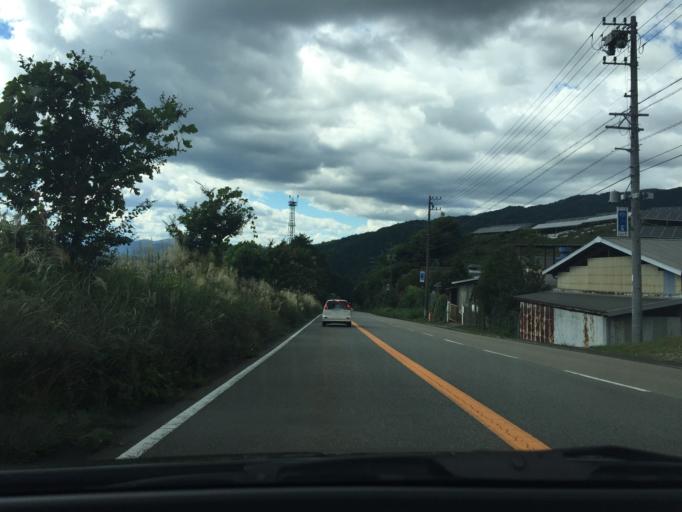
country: JP
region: Gifu
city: Nakatsugawa
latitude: 35.7588
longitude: 137.3245
